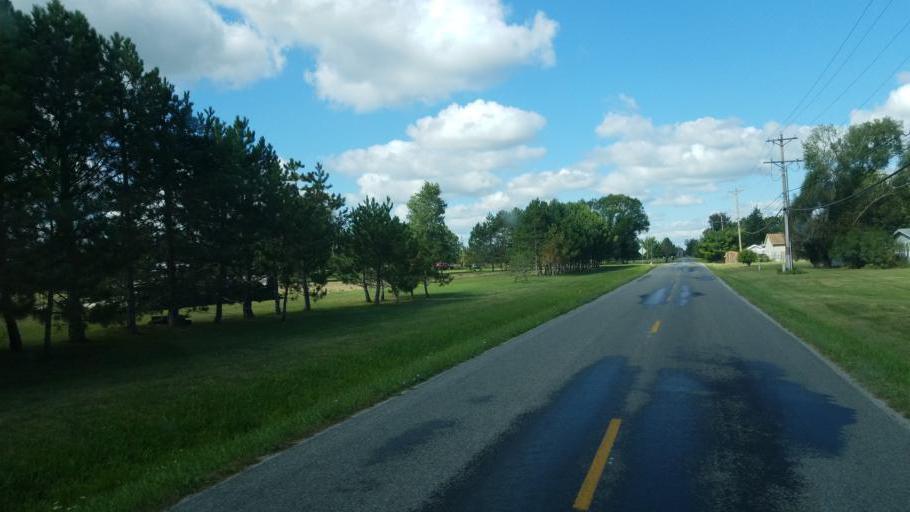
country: US
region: Ohio
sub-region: Lorain County
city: Lagrange
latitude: 41.1998
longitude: -82.1409
